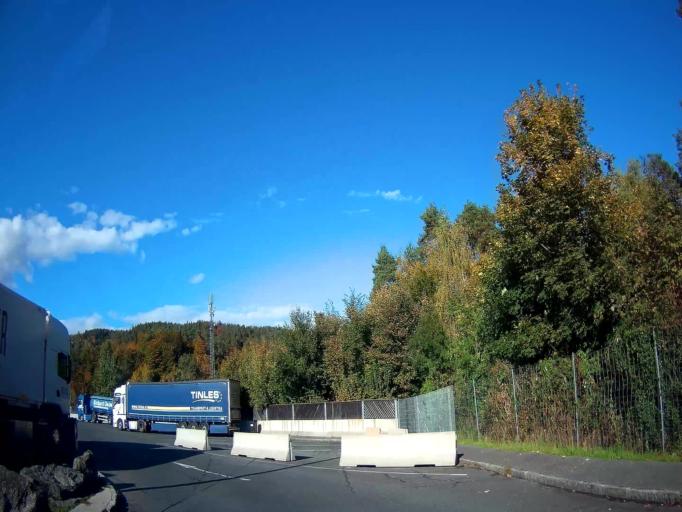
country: AT
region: Carinthia
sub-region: Politischer Bezirk Klagenfurt Land
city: Schiefling am See
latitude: 46.6301
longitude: 14.0960
